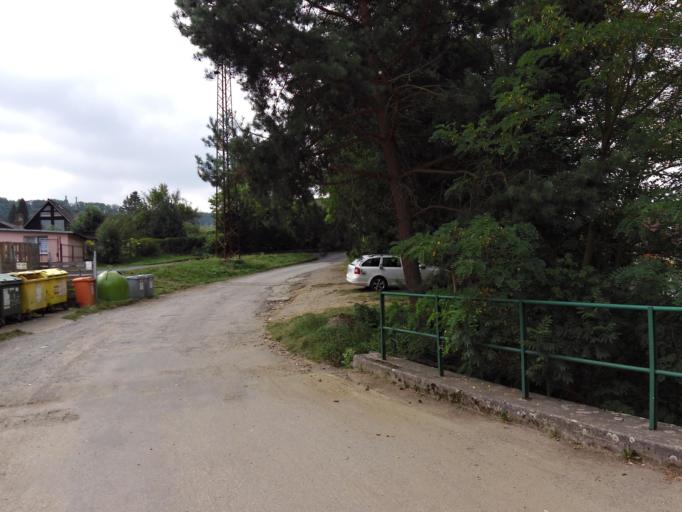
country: CZ
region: Central Bohemia
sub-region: Okres Benesov
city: Cercany
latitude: 49.8733
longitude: 14.7259
